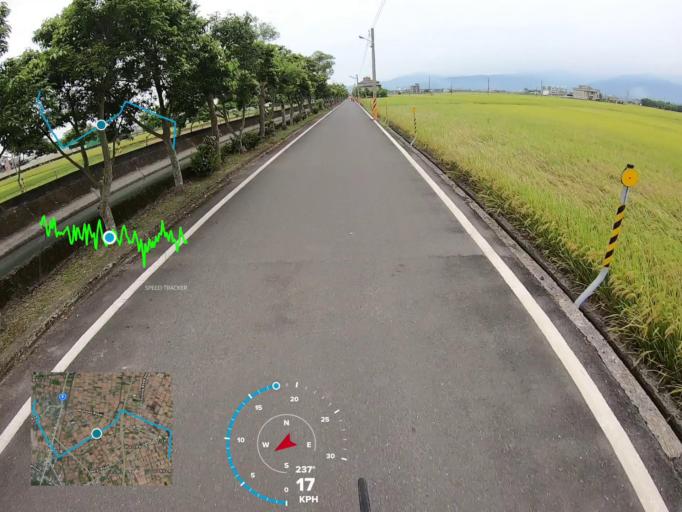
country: TW
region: Taiwan
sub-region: Yilan
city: Yilan
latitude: 24.7796
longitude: 121.7721
